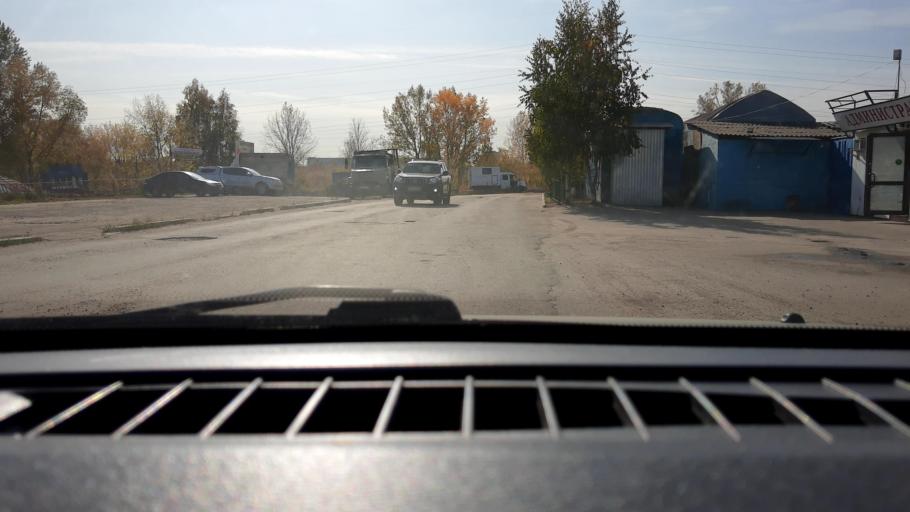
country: RU
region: Nizjnij Novgorod
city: Nizhniy Novgorod
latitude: 56.3439
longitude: 43.8997
